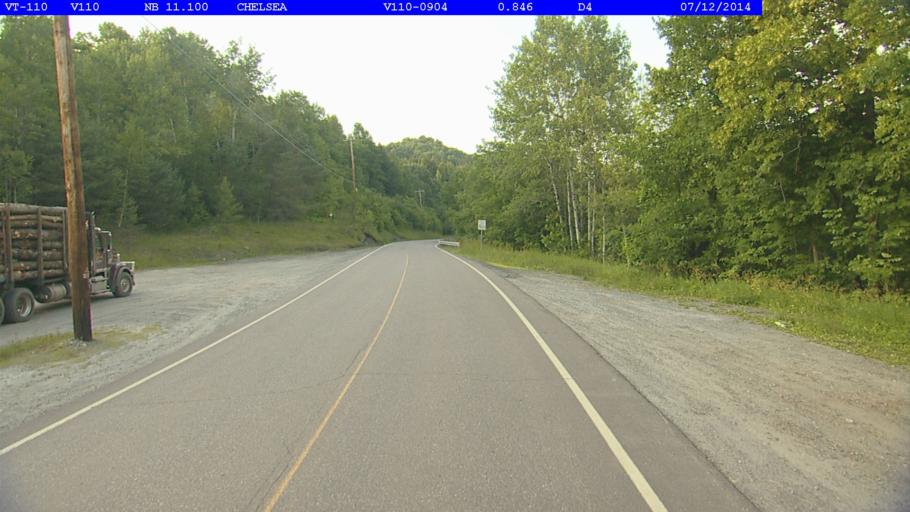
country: US
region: Vermont
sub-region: Orange County
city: Chelsea
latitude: 43.9629
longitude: -72.4638
